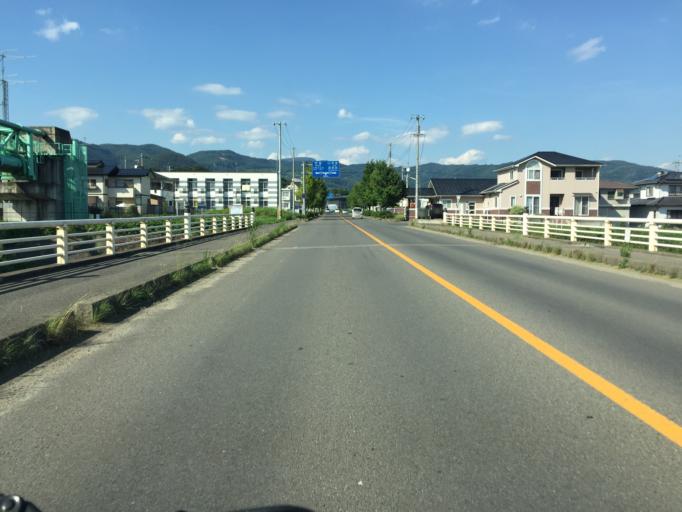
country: JP
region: Fukushima
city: Fukushima-shi
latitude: 37.8243
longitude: 140.4448
